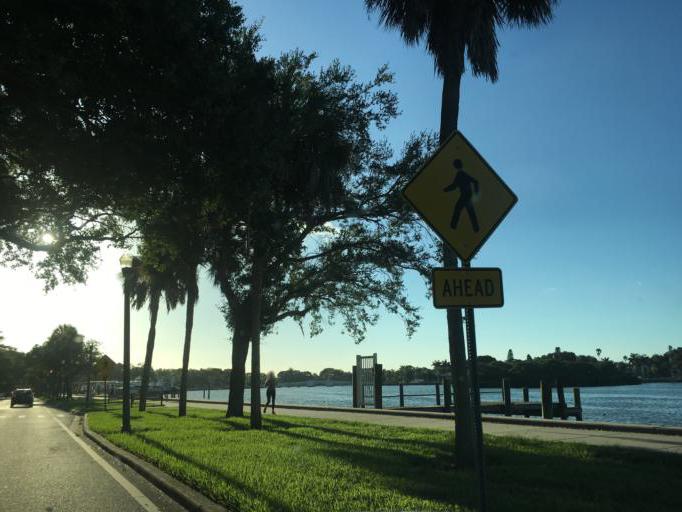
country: US
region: Florida
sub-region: Pinellas County
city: Saint Petersburg
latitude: 27.7894
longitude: -82.6230
